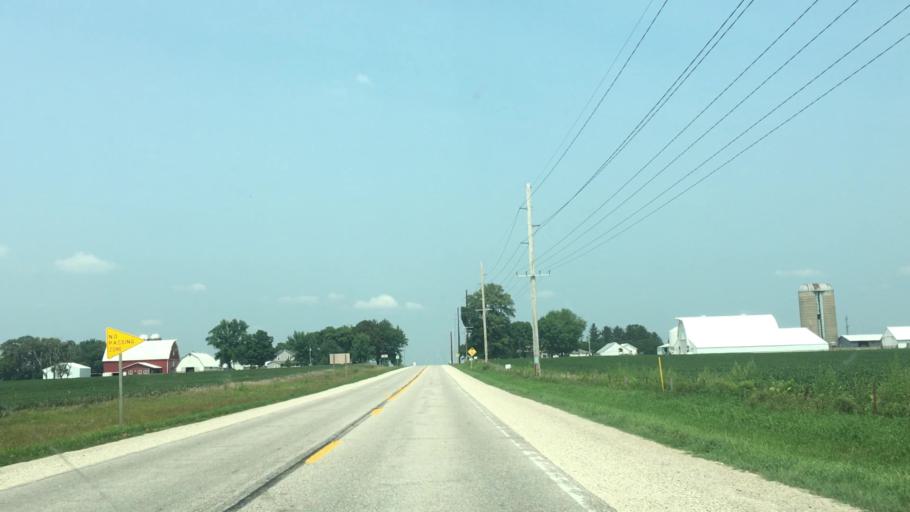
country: US
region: Iowa
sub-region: Buchanan County
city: Independence
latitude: 42.4396
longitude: -91.8900
